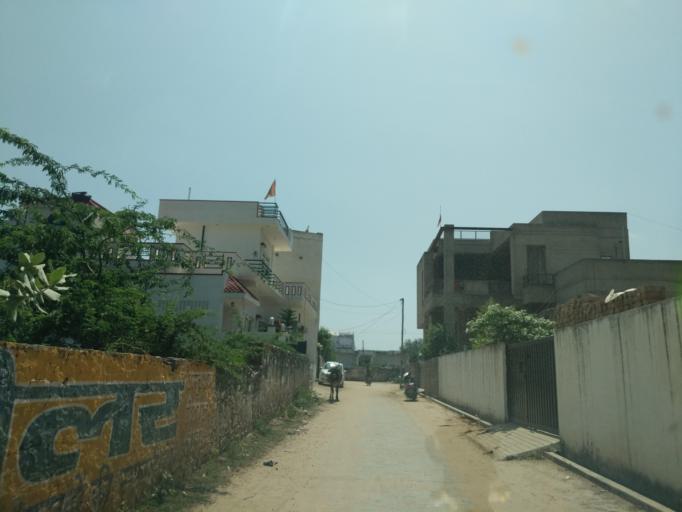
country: IN
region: Rajasthan
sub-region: Nagaur
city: Makrana
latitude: 27.0275
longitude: 74.7527
